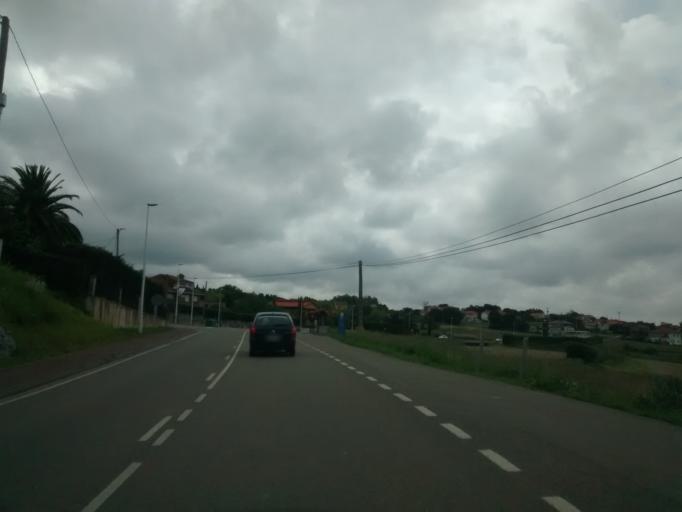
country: ES
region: Cantabria
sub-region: Provincia de Cantabria
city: Santander
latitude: 43.4243
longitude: -3.7665
